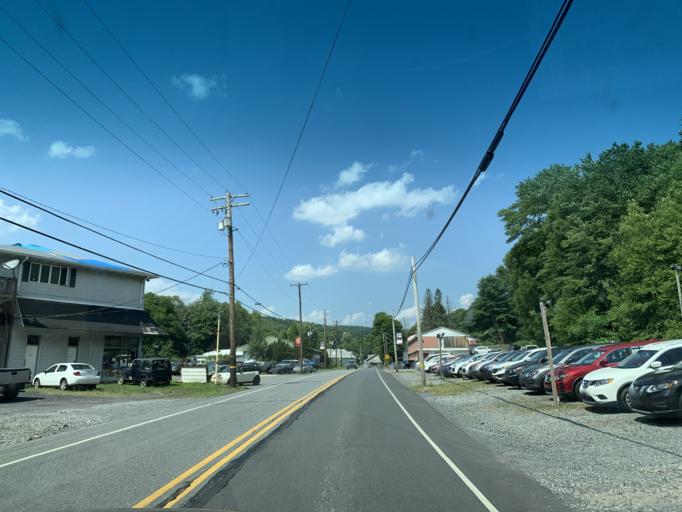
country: US
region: Pennsylvania
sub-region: Schuylkill County
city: Ashland
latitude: 40.7777
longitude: -76.3386
